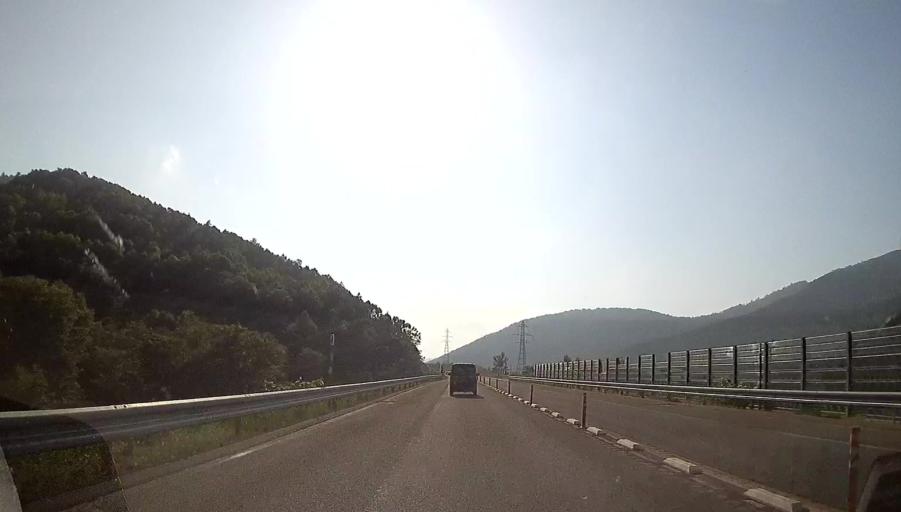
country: JP
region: Hokkaido
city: Shimo-furano
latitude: 43.0534
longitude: 142.6116
